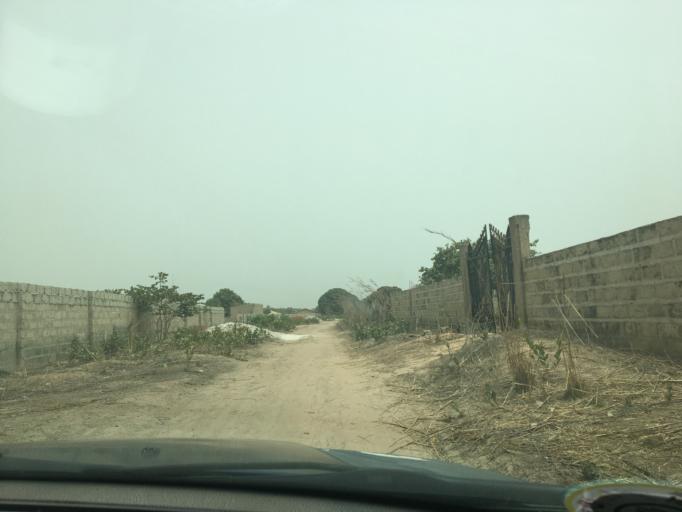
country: GM
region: Western
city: Sukuta
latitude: 13.3136
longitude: -16.7725
